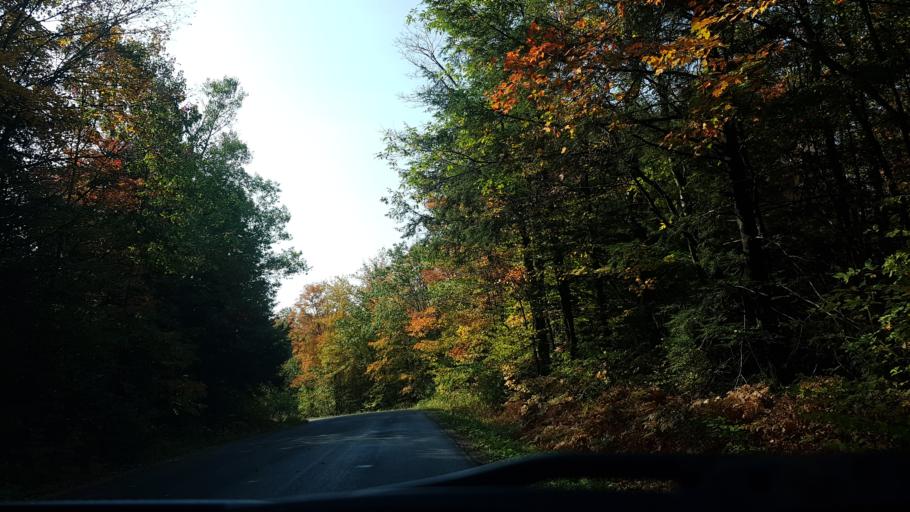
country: CA
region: Ontario
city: Bracebridge
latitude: 44.9725
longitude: -79.2585
